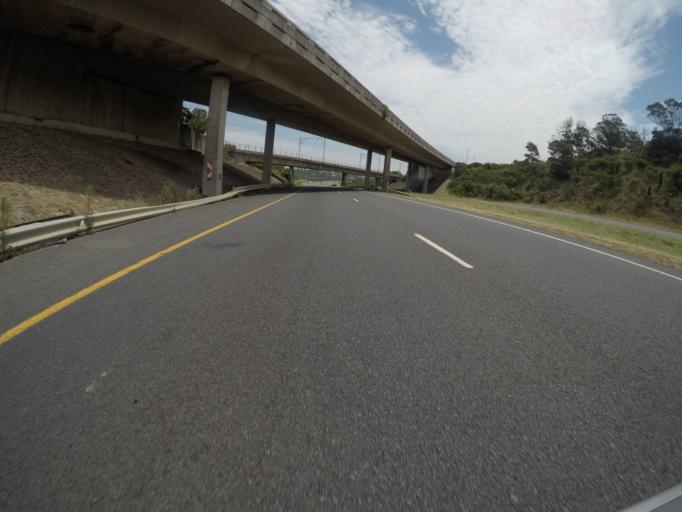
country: ZA
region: Eastern Cape
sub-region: Buffalo City Metropolitan Municipality
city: East London
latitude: -32.9702
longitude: 27.8657
